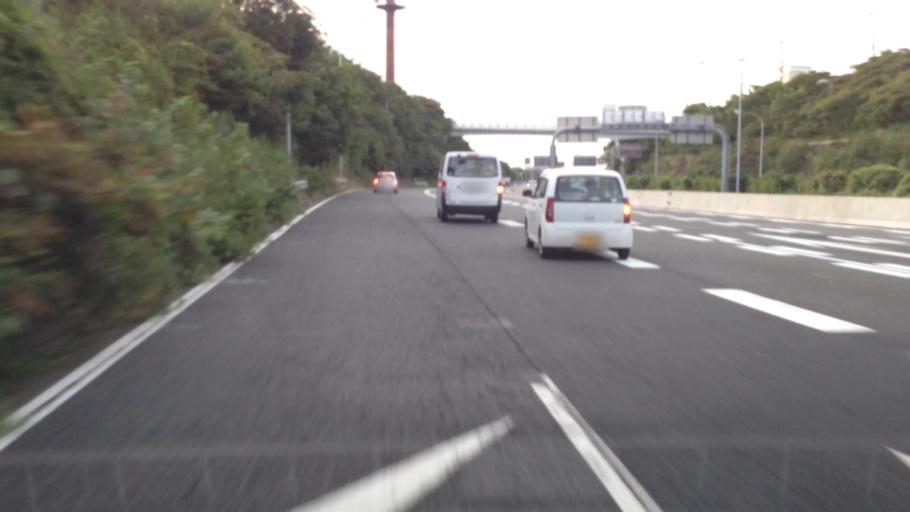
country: JP
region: Kanagawa
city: Yokohama
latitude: 35.4796
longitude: 139.5959
